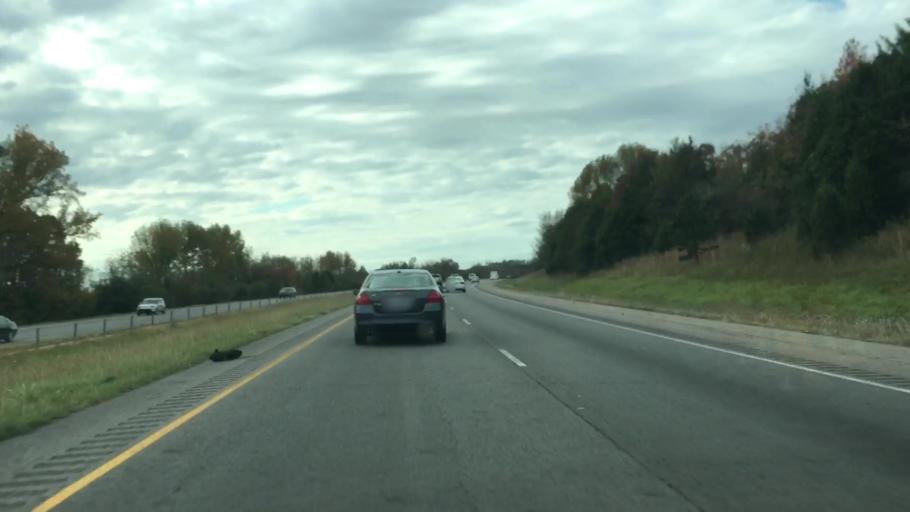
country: US
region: Arkansas
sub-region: Conway County
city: Morrilton
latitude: 35.1634
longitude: -92.6772
